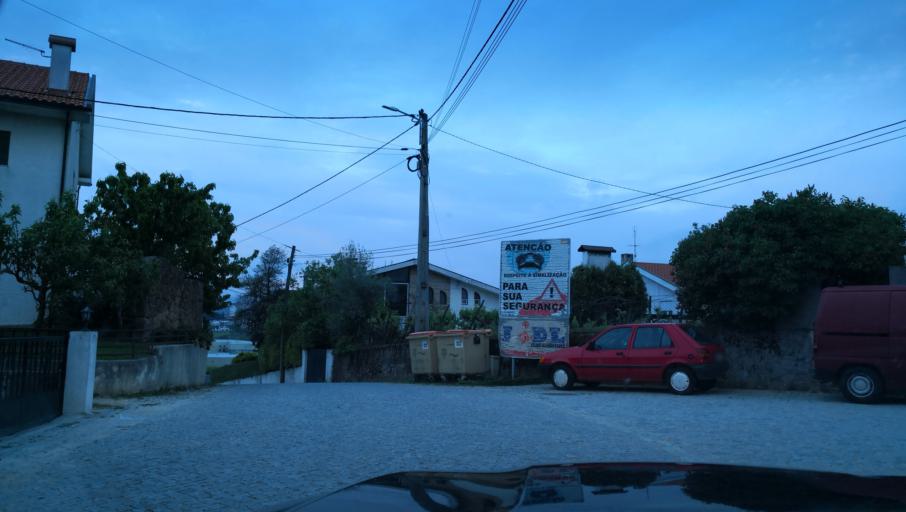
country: PT
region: Vila Real
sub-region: Vila Real
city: Vila Real
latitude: 41.2973
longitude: -7.7248
